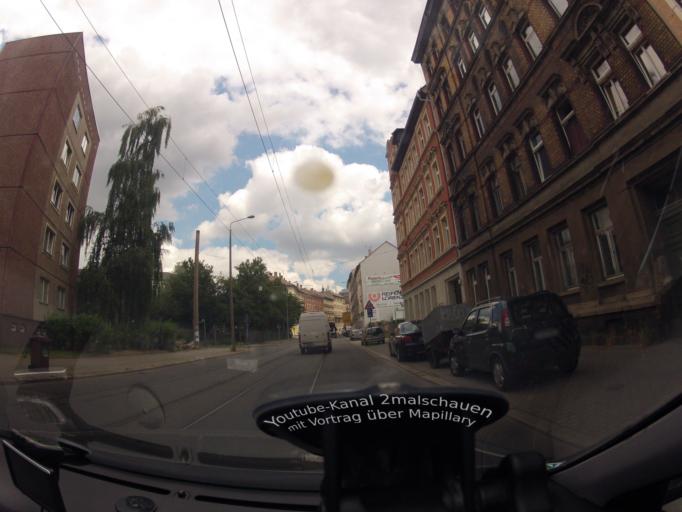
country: DE
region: Saxony
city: Leipzig
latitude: 51.3432
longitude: 12.4122
